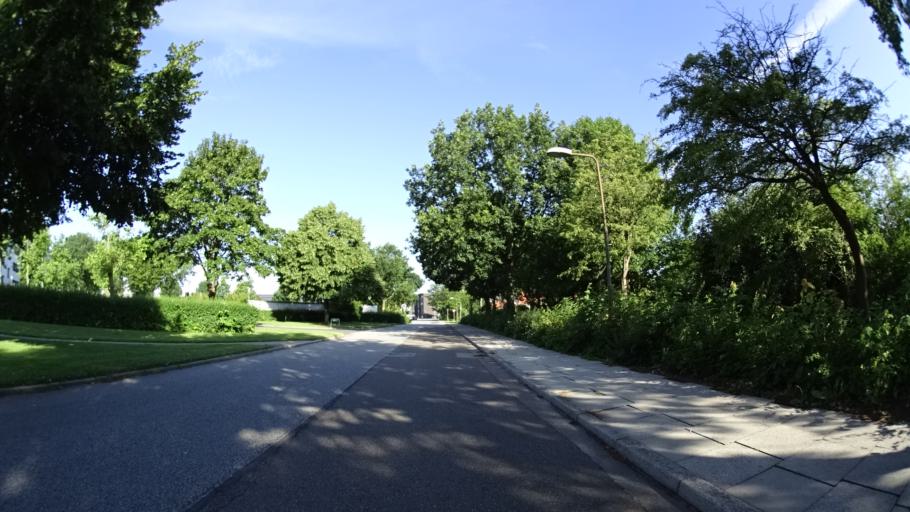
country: DK
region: Central Jutland
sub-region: Arhus Kommune
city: Stavtrup
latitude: 56.1173
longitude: 10.1587
